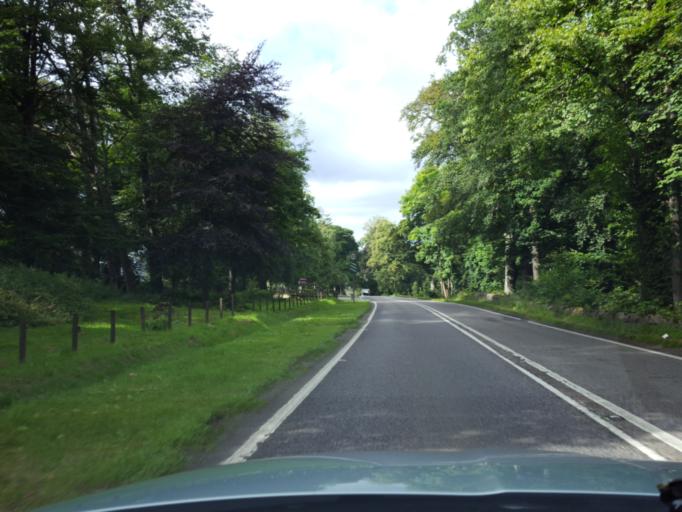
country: GB
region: Scotland
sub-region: Moray
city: Rothes
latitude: 57.4774
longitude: -3.2098
